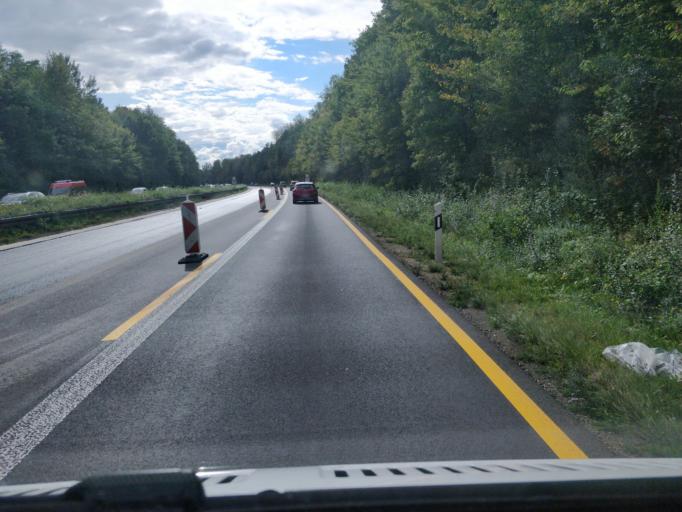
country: DE
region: North Rhine-Westphalia
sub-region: Regierungsbezirk Koln
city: Frechen
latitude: 50.8850
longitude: 6.8070
